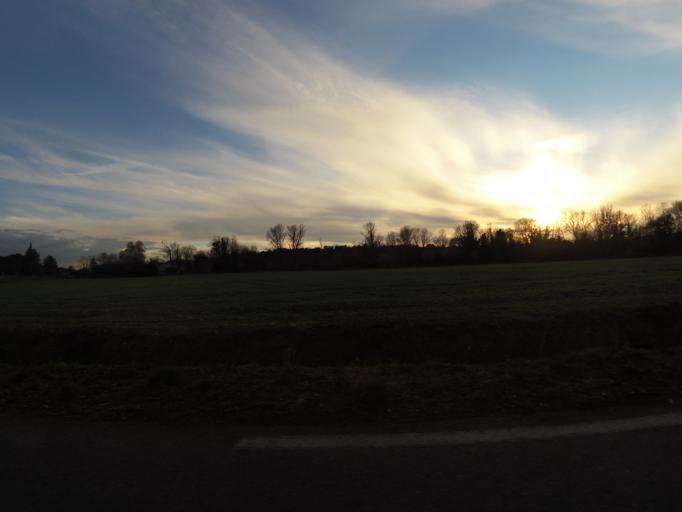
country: FR
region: Languedoc-Roussillon
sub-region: Departement du Gard
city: Saint-Mamert-du-Gard
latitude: 43.8704
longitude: 4.2126
